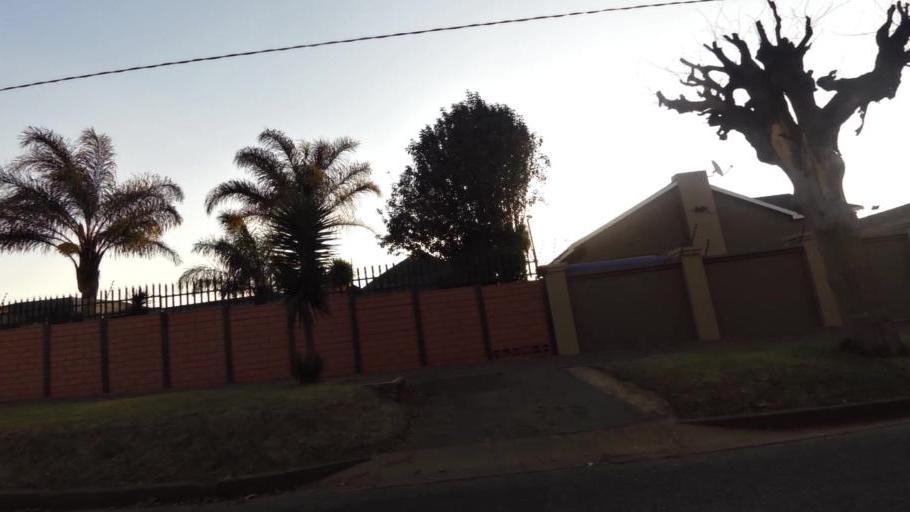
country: ZA
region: Gauteng
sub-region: City of Johannesburg Metropolitan Municipality
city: Johannesburg
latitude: -26.1782
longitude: 27.9619
